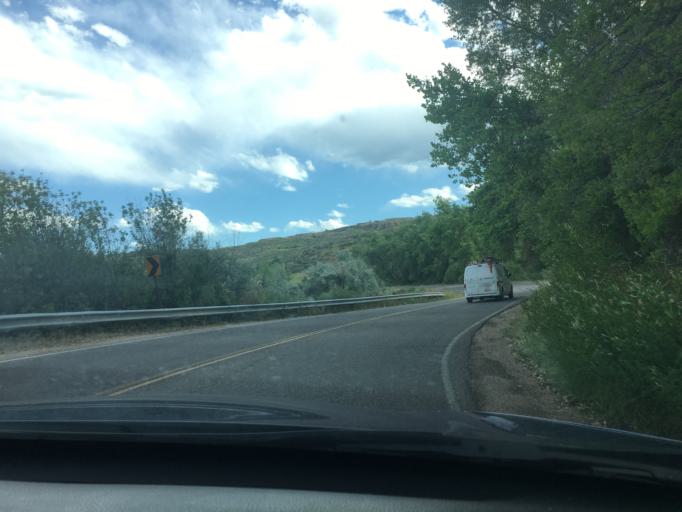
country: US
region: Colorado
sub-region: Jefferson County
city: Applewood
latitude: 39.7642
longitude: -105.1823
